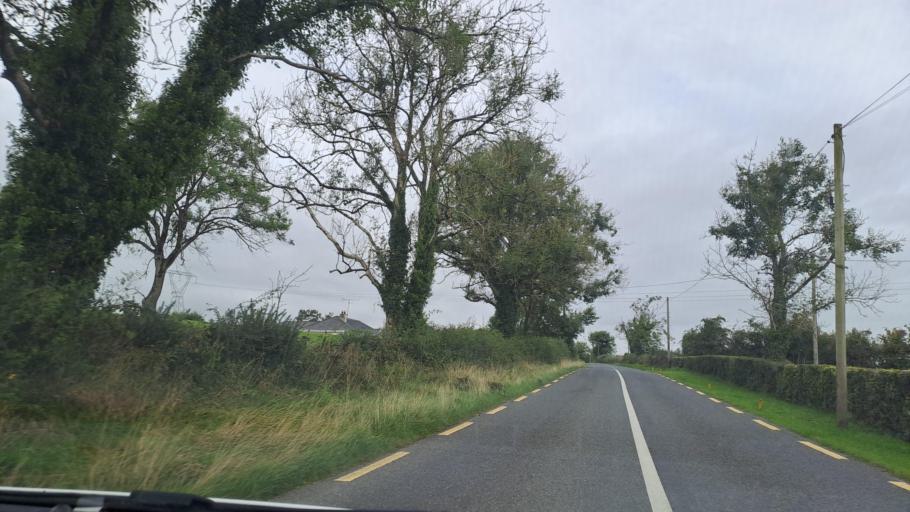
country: IE
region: Ulster
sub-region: An Cabhan
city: Kingscourt
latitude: 53.8755
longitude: -6.7163
